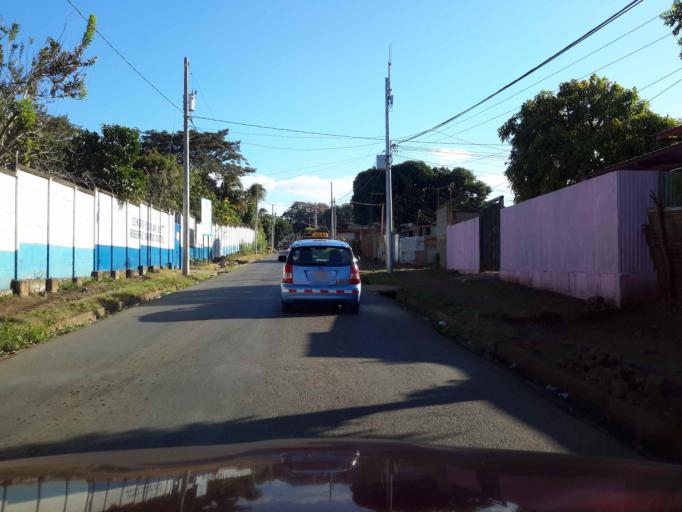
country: NI
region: Managua
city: Managua
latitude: 12.1142
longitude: -86.2936
